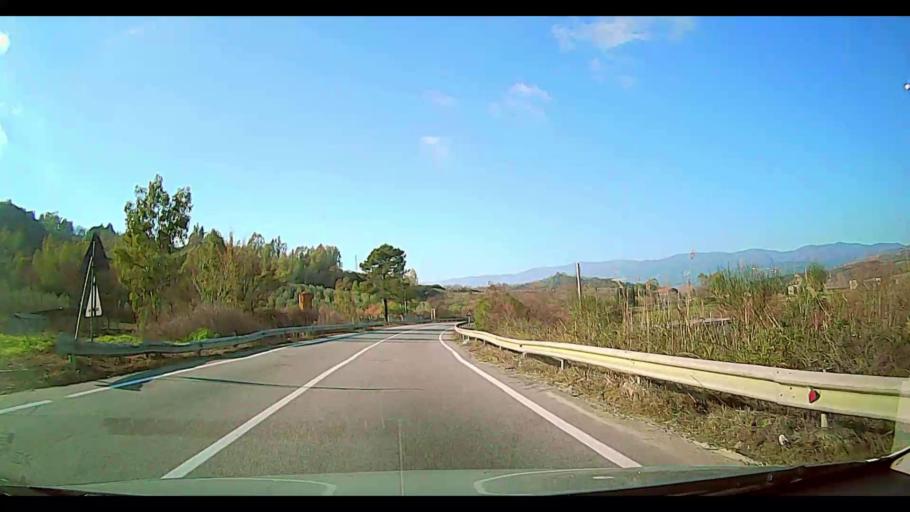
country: IT
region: Calabria
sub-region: Provincia di Crotone
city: Belvedere Spinello
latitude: 39.1896
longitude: 16.8776
